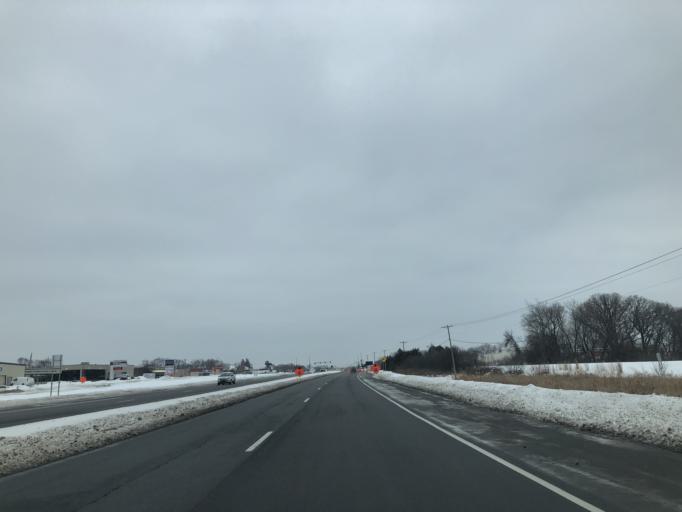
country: US
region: Minnesota
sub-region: Hennepin County
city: Brooklyn Park
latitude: 45.0910
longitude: -93.3821
